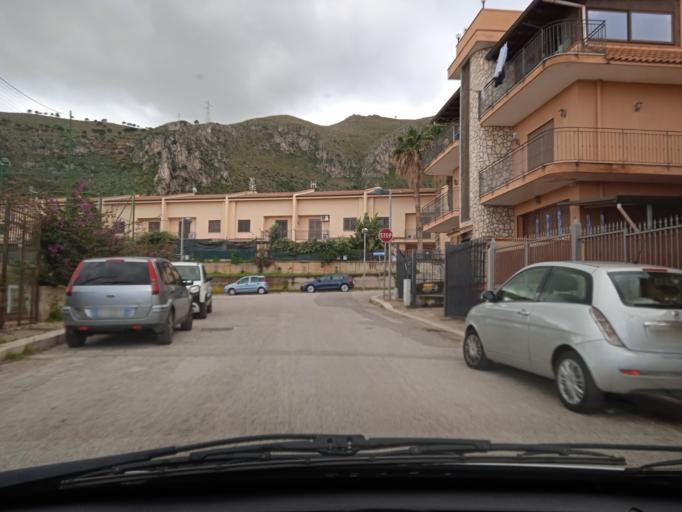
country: IT
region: Sicily
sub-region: Palermo
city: Villabate
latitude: 38.0738
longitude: 13.4400
